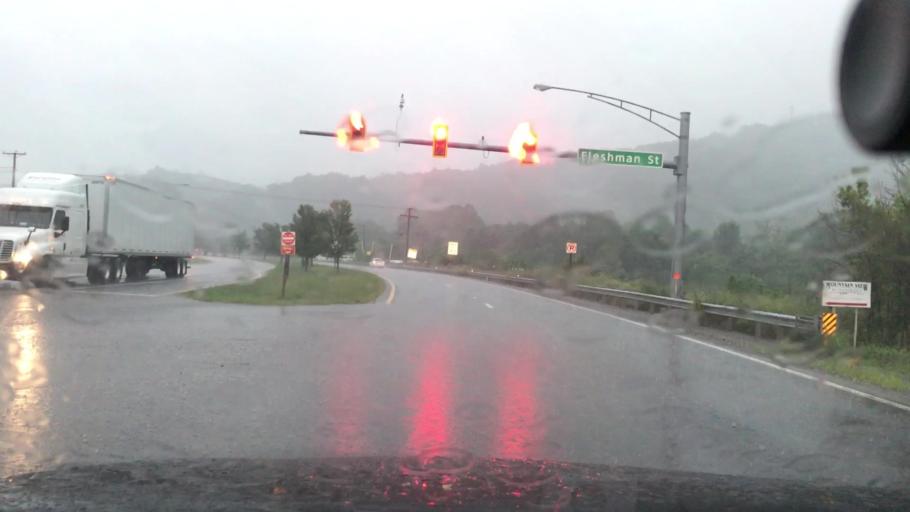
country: US
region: Virginia
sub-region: Giles County
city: Narrows
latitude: 37.3347
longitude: -80.8055
